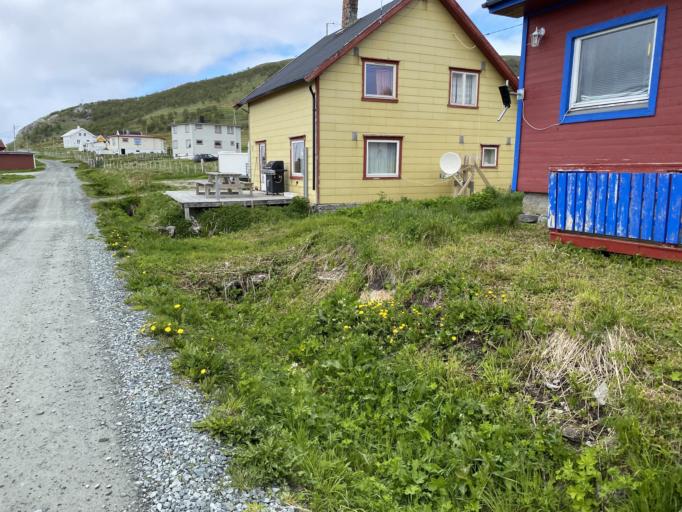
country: NO
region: Troms
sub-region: Karlsoy
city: Hansnes
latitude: 70.0021
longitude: 19.8917
